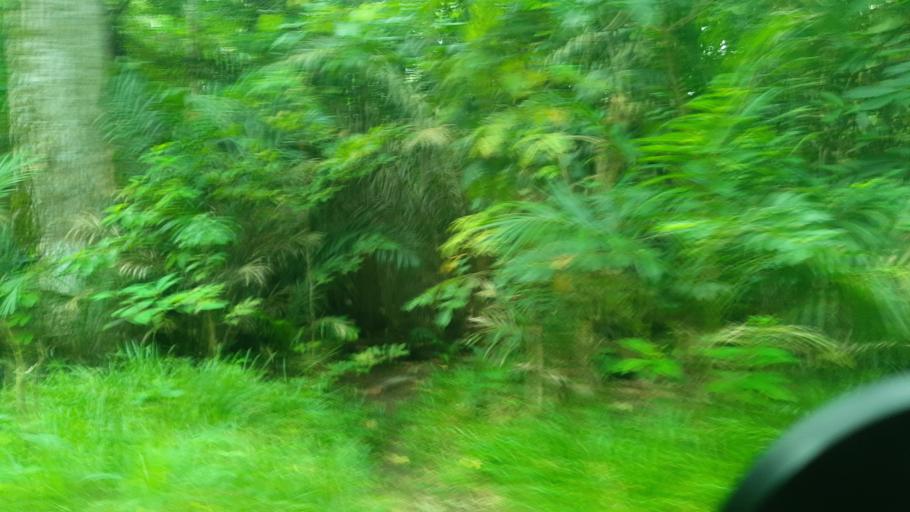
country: ST
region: Sao Tome Island
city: Sao Tome
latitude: 0.2431
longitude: 6.7442
